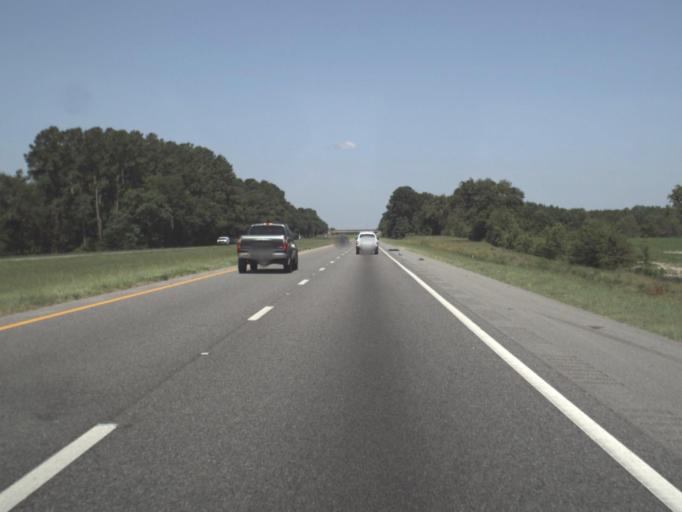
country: US
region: Florida
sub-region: Suwannee County
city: Live Oak
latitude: 30.3508
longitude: -83.0143
